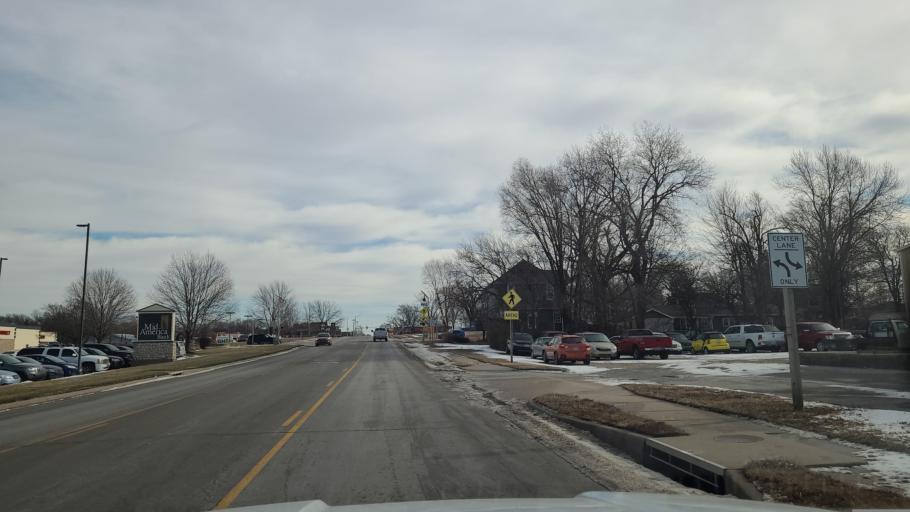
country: US
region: Kansas
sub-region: Douglas County
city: Baldwin City
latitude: 38.7822
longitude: -95.1902
